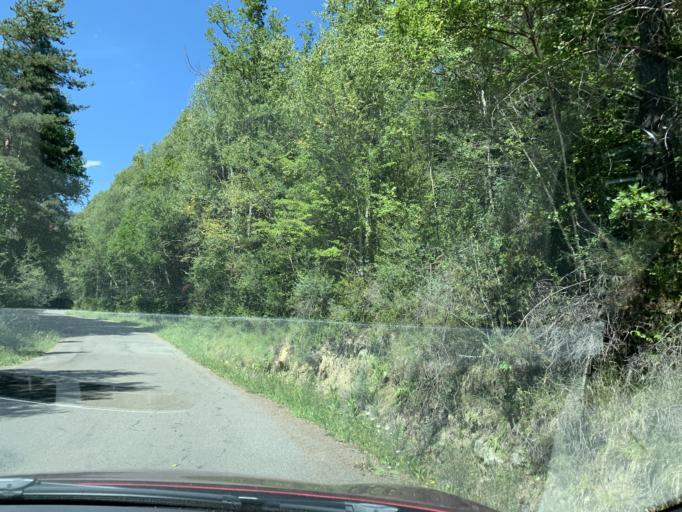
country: ES
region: Aragon
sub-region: Provincia de Huesca
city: Hoz de Jaca
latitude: 42.6995
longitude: -0.3080
